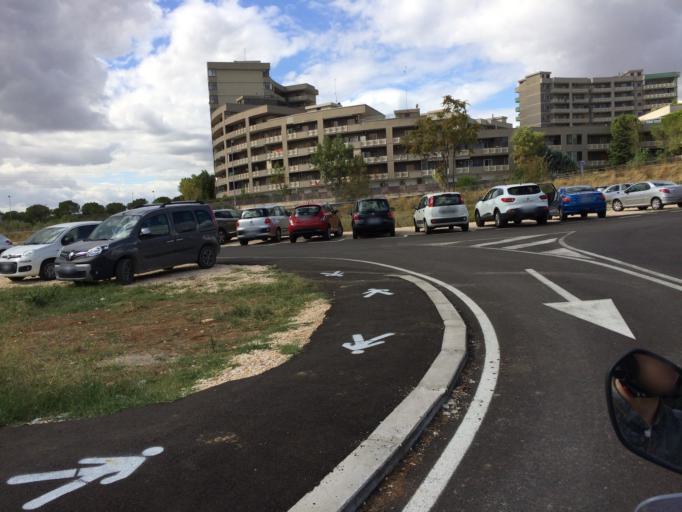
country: IT
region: Apulia
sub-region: Provincia di Bari
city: Bari
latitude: 41.0930
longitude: 16.8579
